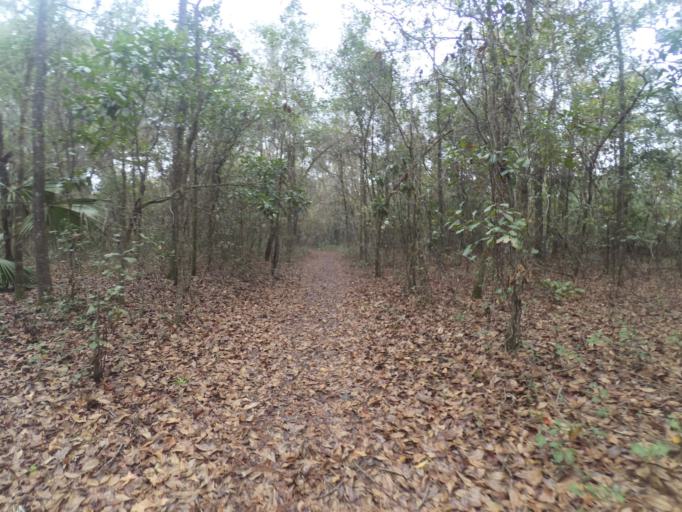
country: US
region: Florida
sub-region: Alachua County
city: Gainesville
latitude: 29.5428
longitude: -82.2728
